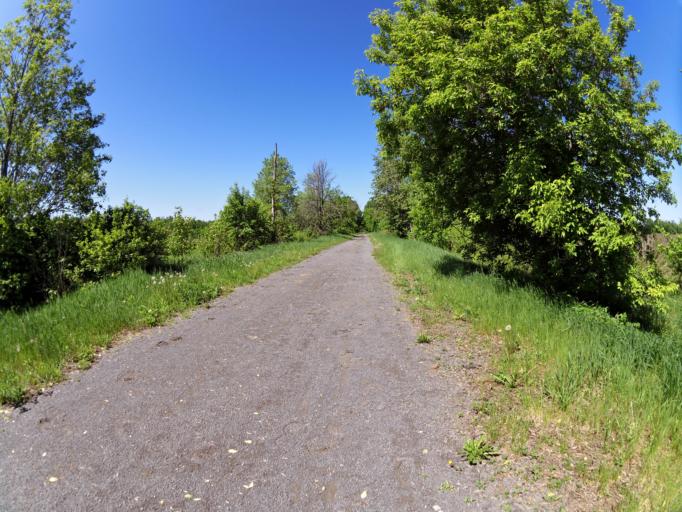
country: CA
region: Ontario
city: Clarence-Rockland
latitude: 45.4271
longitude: -75.3091
